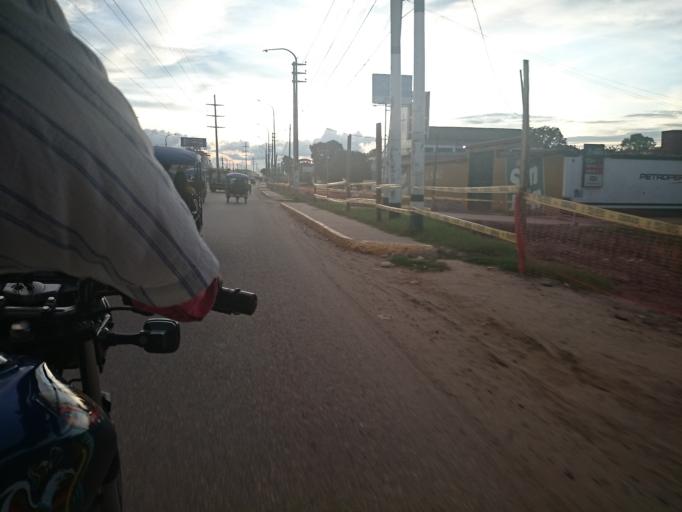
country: PE
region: Ucayali
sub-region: Provincia de Coronel Portillo
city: Pucallpa
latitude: -8.3848
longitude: -74.5495
